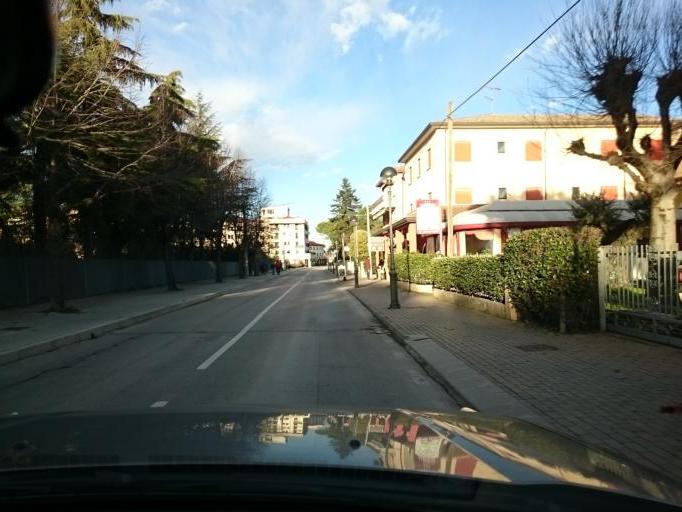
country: IT
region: Veneto
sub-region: Provincia di Padova
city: Montegrotto Terme
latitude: 45.3254
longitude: 11.7935
